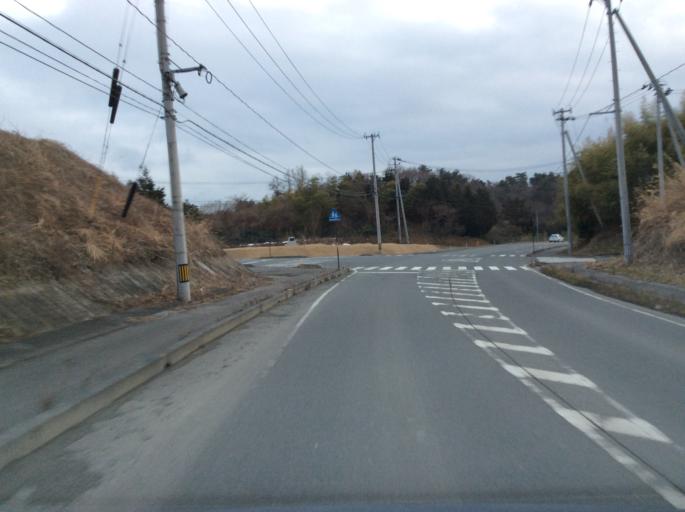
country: JP
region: Fukushima
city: Iwaki
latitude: 37.1205
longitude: 140.9793
